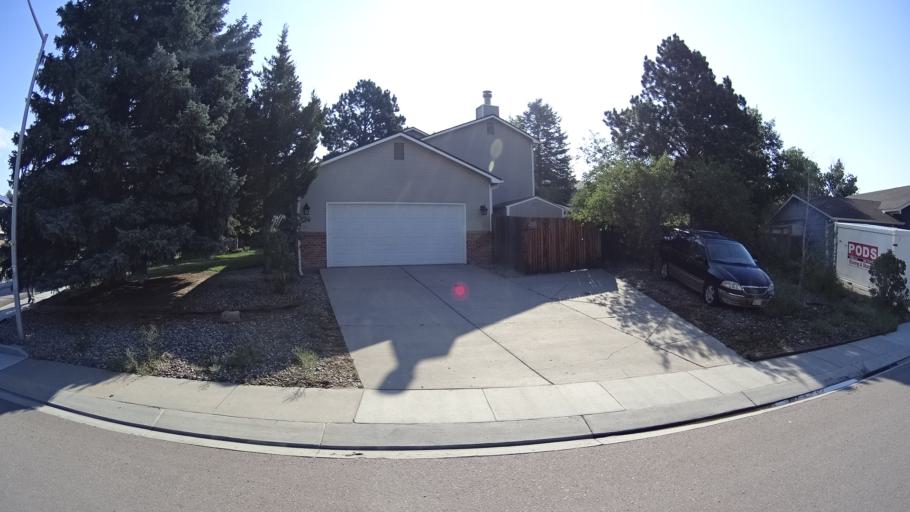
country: US
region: Colorado
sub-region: El Paso County
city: Air Force Academy
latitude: 38.9454
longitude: -104.7792
